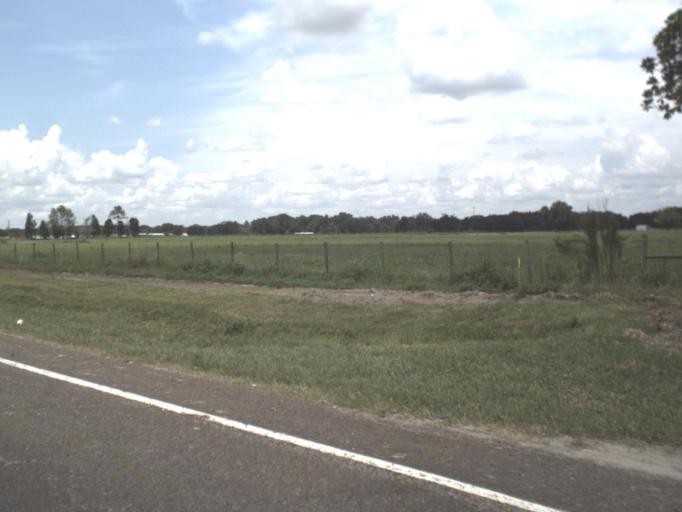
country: US
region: Florida
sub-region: Hillsborough County
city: Plant City
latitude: 27.9417
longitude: -82.1210
